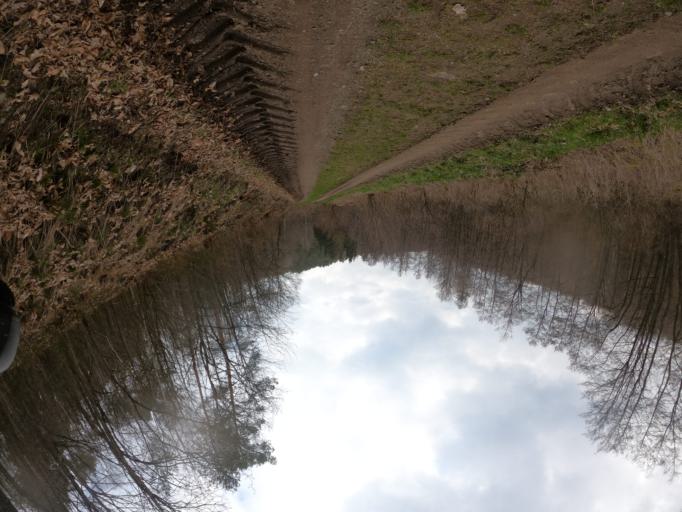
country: DE
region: North Rhine-Westphalia
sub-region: Regierungsbezirk Koln
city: Hurtgenwald
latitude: 50.7014
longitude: 6.3856
